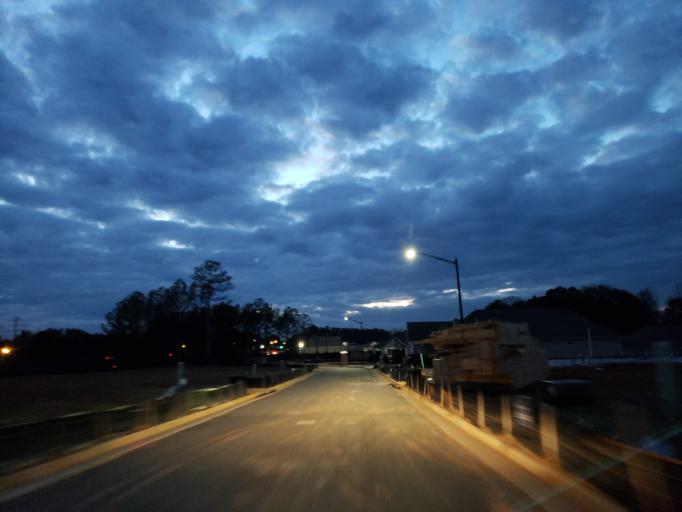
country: US
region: Georgia
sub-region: Cobb County
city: Kennesaw
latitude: 33.9988
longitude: -84.6467
